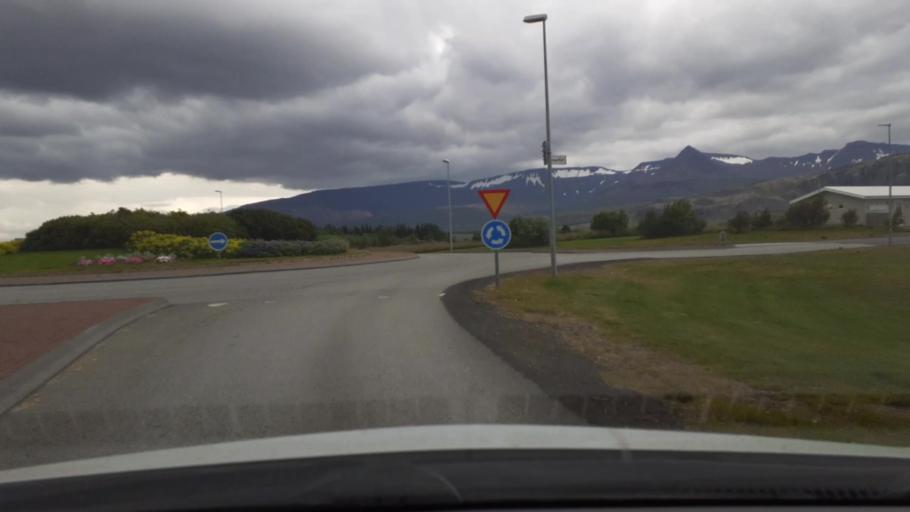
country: IS
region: West
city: Borgarnes
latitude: 64.5608
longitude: -21.7629
